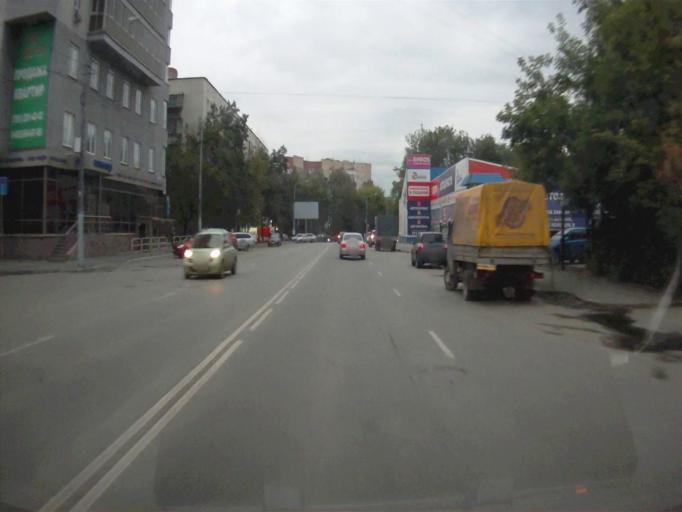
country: RU
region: Chelyabinsk
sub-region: Gorod Chelyabinsk
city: Chelyabinsk
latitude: 55.1525
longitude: 61.3984
